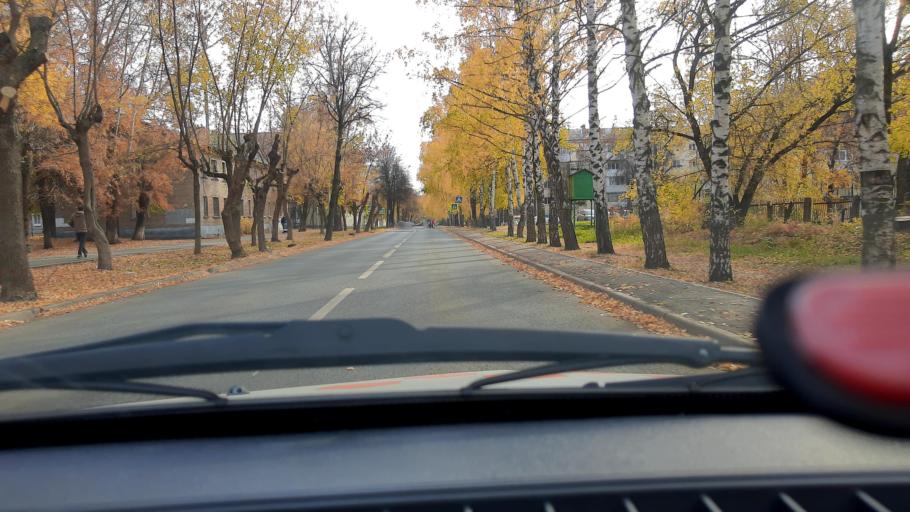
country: RU
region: Bashkortostan
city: Ufa
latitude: 54.8104
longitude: 56.1106
